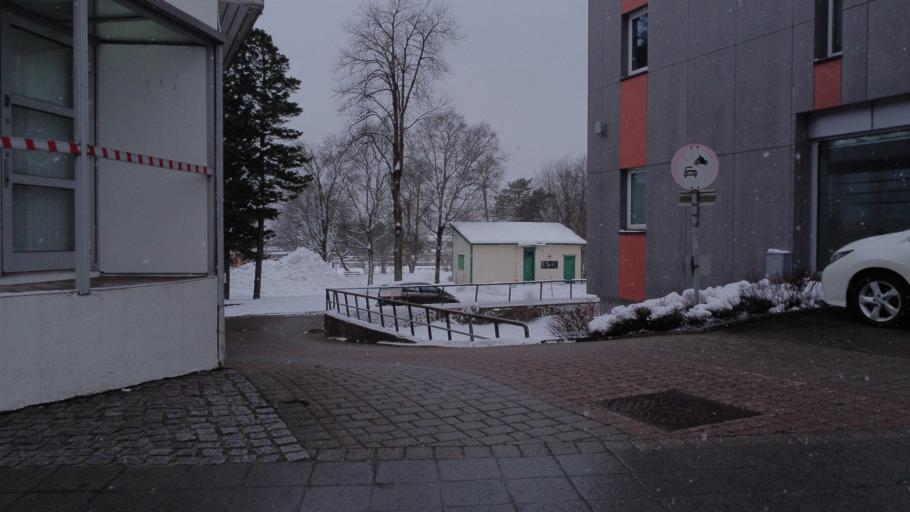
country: NO
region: Nordland
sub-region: Rana
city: Mo i Rana
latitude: 66.3118
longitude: 14.1371
